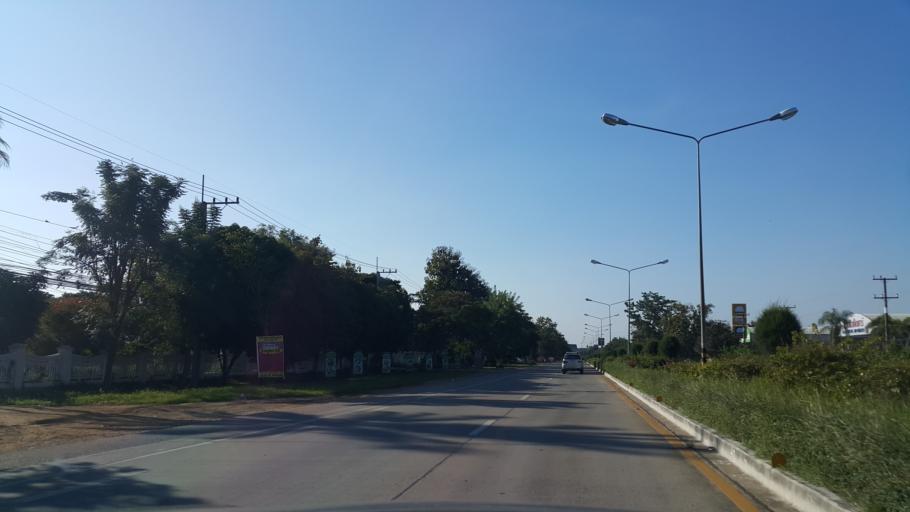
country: TH
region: Lamphun
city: Lamphun
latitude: 18.5641
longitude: 99.0308
